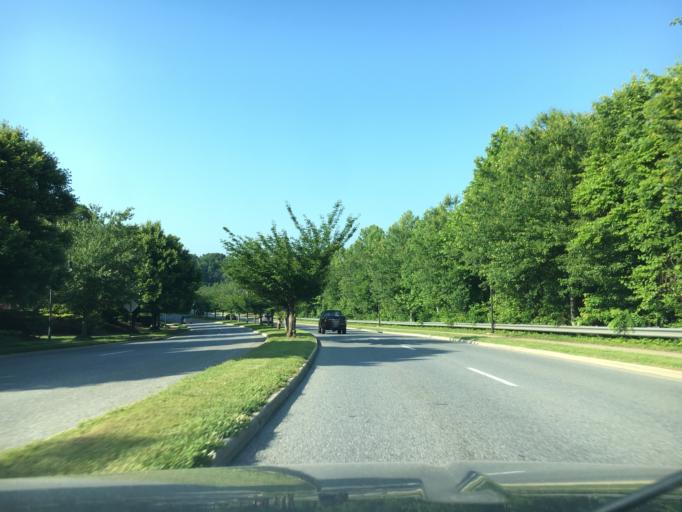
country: US
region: Virginia
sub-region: Campbell County
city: Timberlake
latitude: 37.3516
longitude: -79.2420
